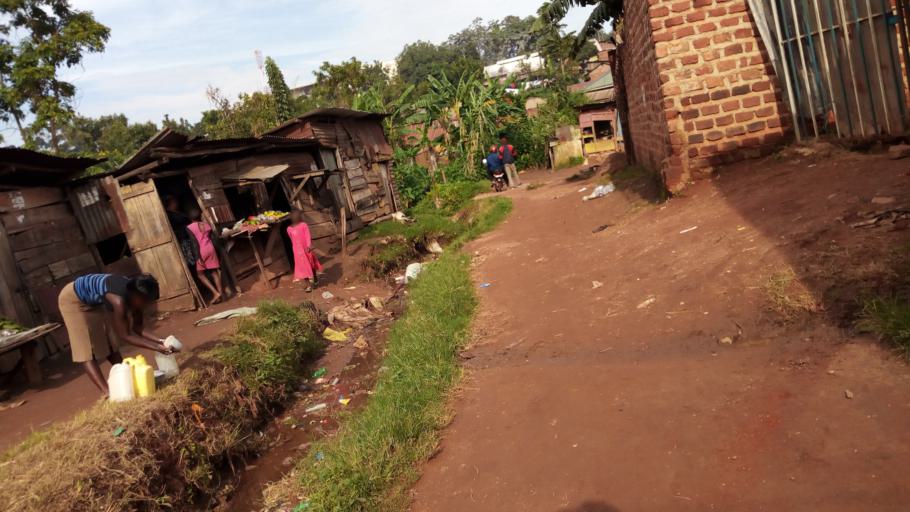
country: UG
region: Central Region
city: Kampala Central Division
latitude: 0.3708
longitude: 32.5560
